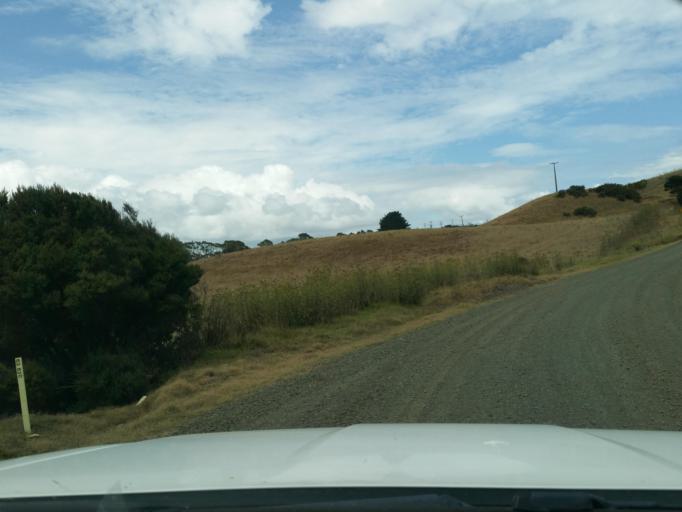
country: NZ
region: Auckland
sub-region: Auckland
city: Wellsford
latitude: -36.3490
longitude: 174.1716
